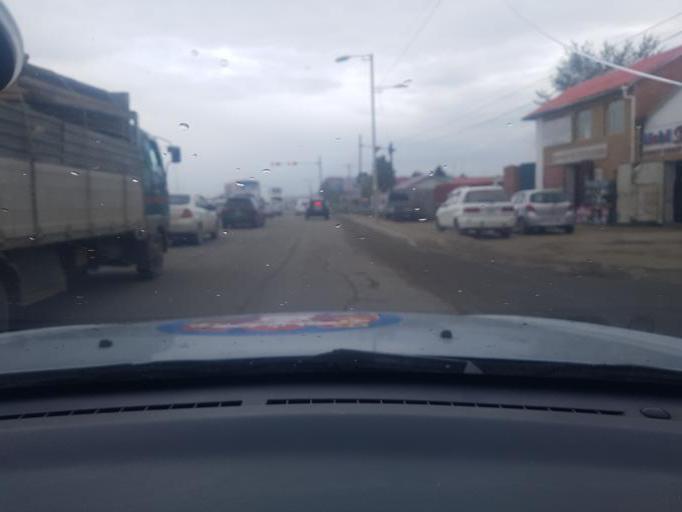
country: MN
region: Ulaanbaatar
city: Ulaanbaatar
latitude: 47.9097
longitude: 106.8033
